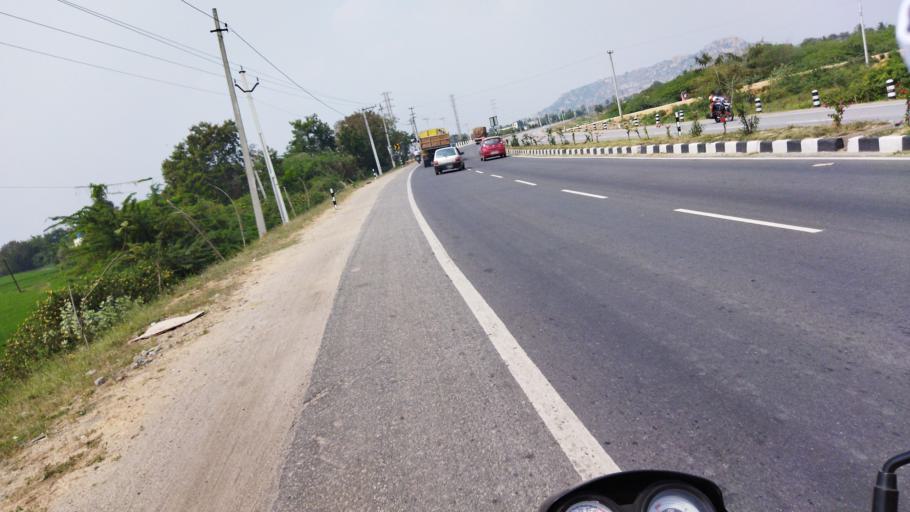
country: IN
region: Telangana
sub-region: Nalgonda
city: Nalgonda
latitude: 17.0795
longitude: 79.2783
